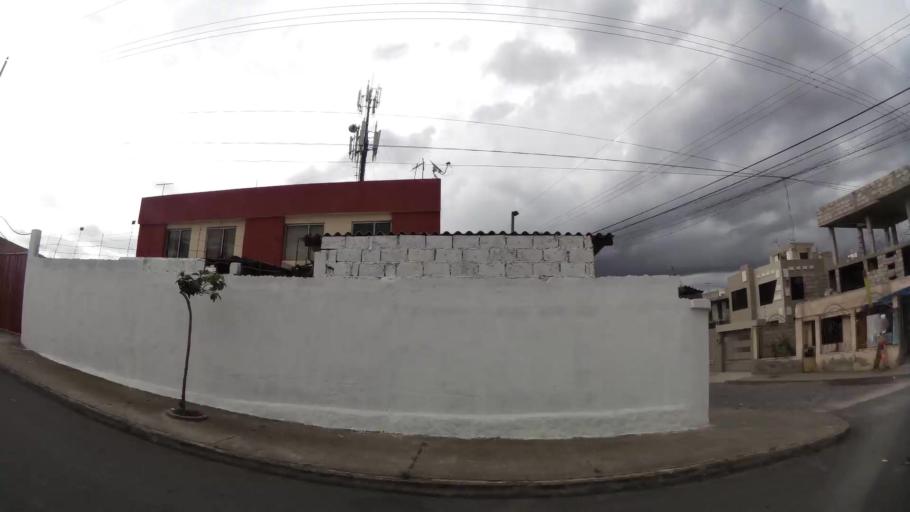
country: EC
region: Tungurahua
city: Ambato
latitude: -1.2767
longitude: -78.6219
